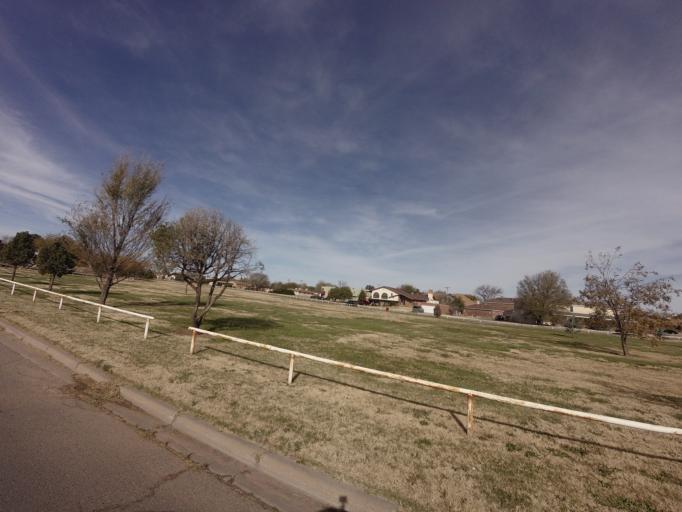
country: US
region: New Mexico
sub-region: Curry County
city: Clovis
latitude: 34.4120
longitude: -103.1926
